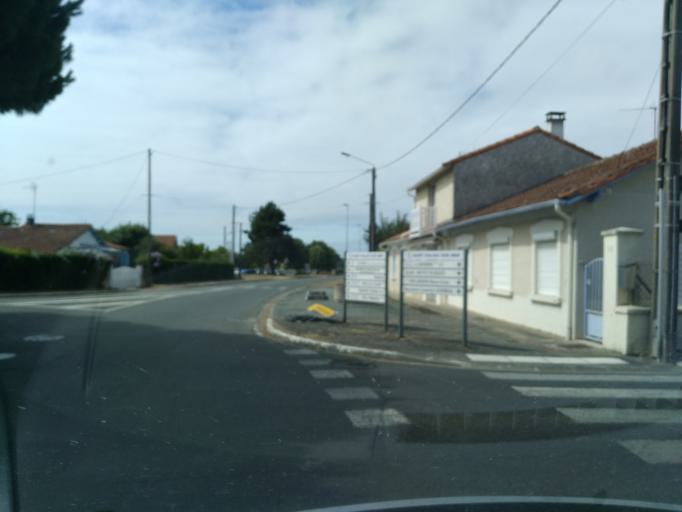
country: FR
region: Poitou-Charentes
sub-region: Departement de la Charente-Maritime
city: Saint-Palais-sur-Mer
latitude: 45.6533
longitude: -1.0786
